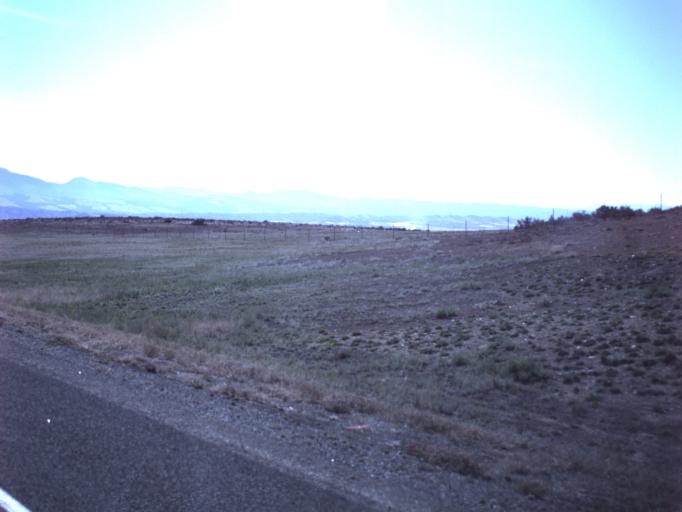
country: US
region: Utah
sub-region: Sanpete County
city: Gunnison
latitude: 39.1692
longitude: -111.8239
